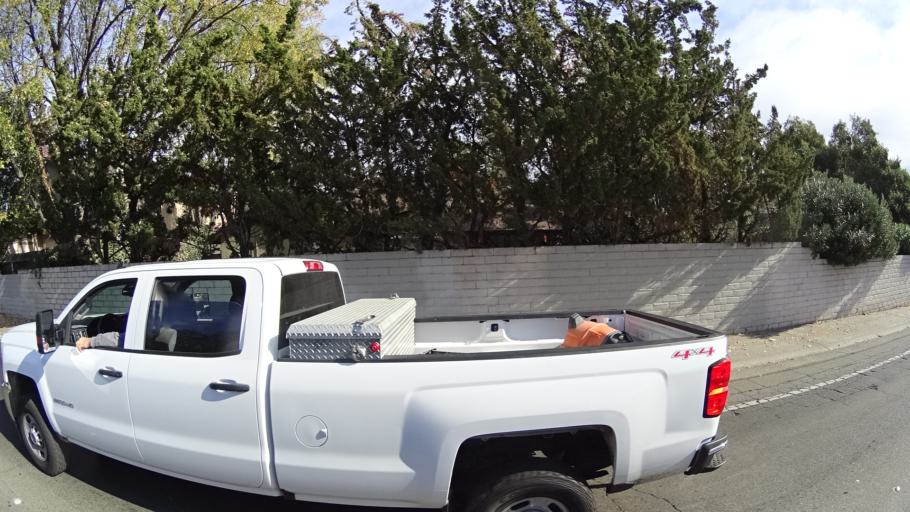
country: US
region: California
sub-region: Sacramento County
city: Fair Oaks
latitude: 38.6704
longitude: -121.2622
